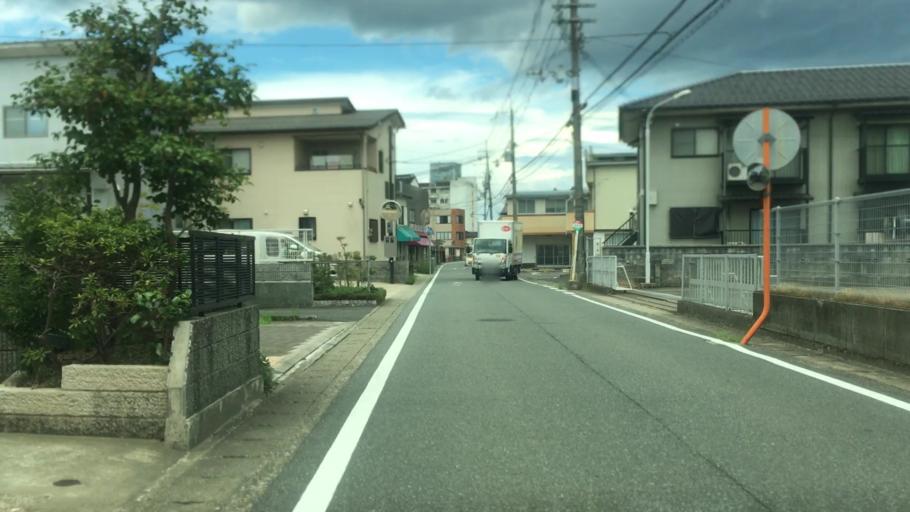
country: JP
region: Hyogo
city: Toyooka
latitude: 35.5305
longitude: 134.8215
